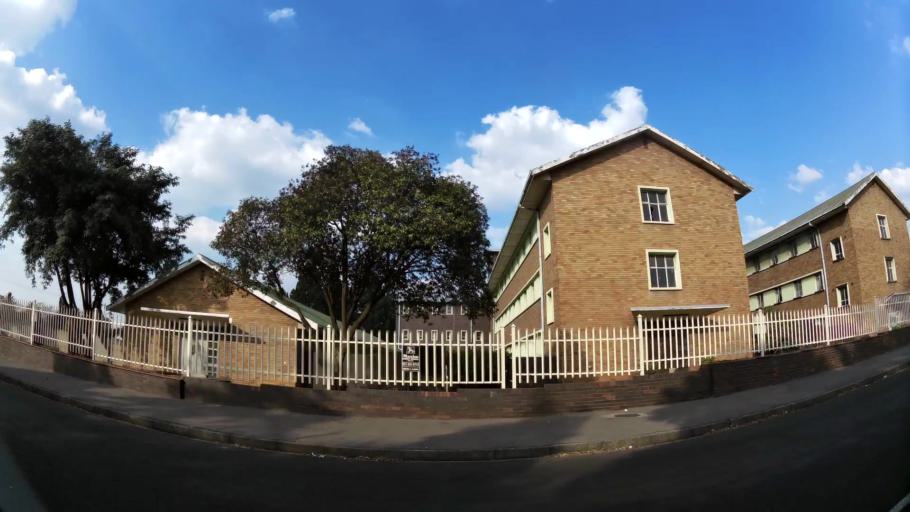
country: ZA
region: Gauteng
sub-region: Ekurhuleni Metropolitan Municipality
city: Germiston
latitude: -26.2394
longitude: 28.1844
